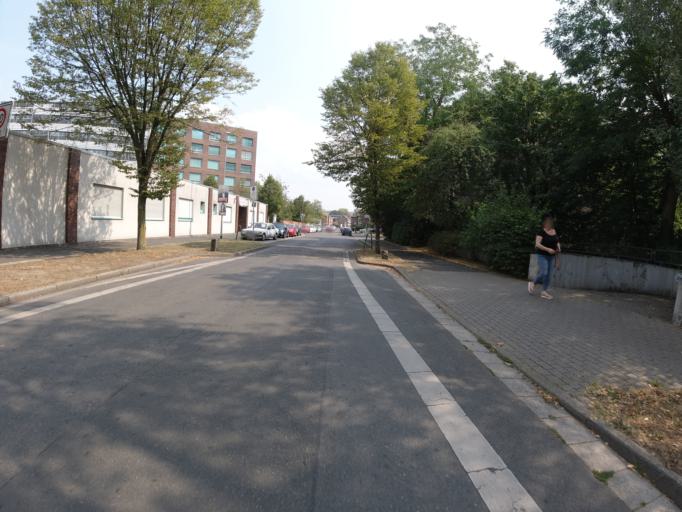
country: DE
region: North Rhine-Westphalia
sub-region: Regierungsbezirk Dusseldorf
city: Moers
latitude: 51.4452
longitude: 6.6387
